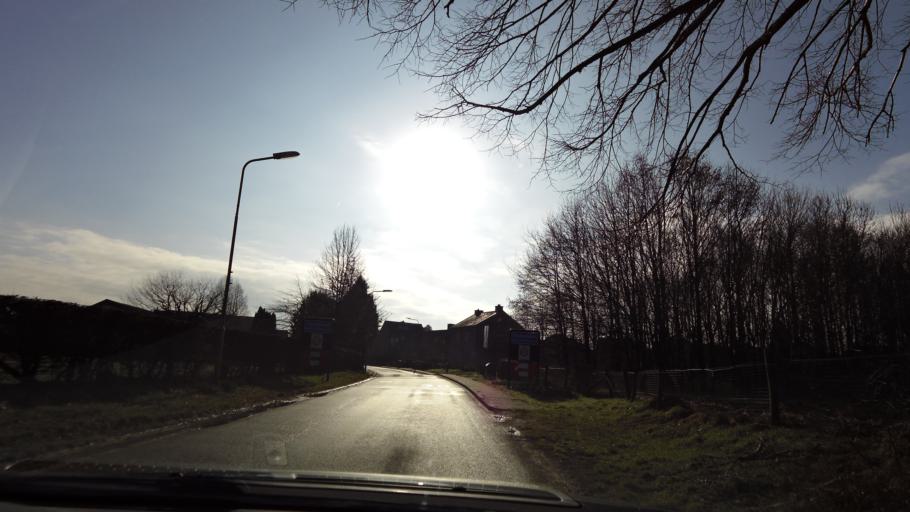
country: NL
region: Limburg
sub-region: Valkenburg aan de Geul
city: Sibbe
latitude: 50.8306
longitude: 5.8384
